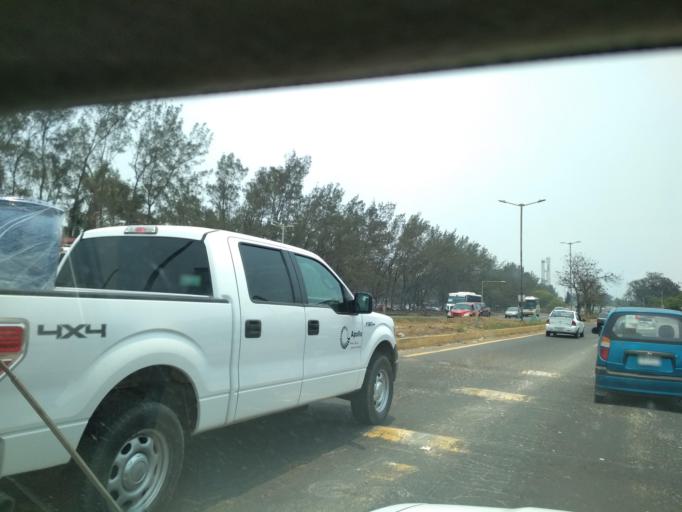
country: MX
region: Veracruz
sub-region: Veracruz
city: Oasis
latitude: 19.1760
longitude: -96.2412
